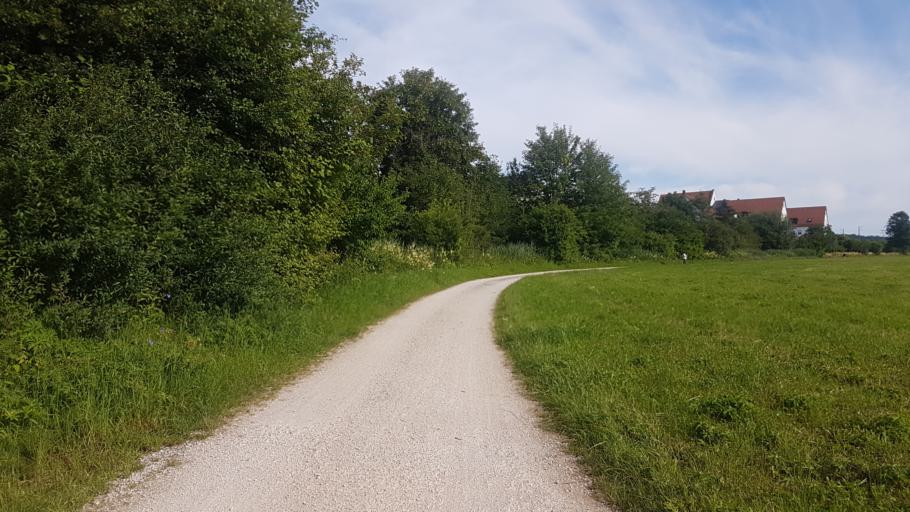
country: DE
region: Bavaria
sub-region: Regierungsbezirk Mittelfranken
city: Treuchtlingen
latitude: 48.9661
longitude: 10.9123
